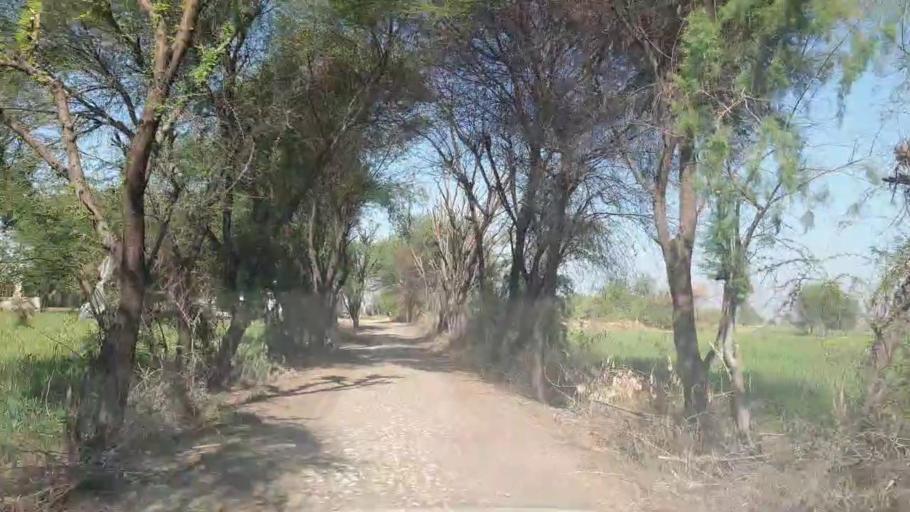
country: PK
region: Sindh
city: Mirpur Khas
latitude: 25.5223
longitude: 69.1878
